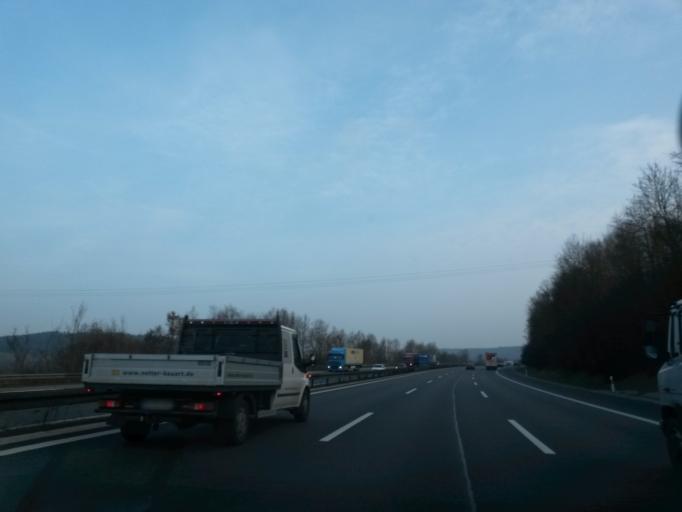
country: DE
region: Bavaria
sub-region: Regierungsbezirk Mittelfranken
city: Greding
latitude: 49.0612
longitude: 11.3227
